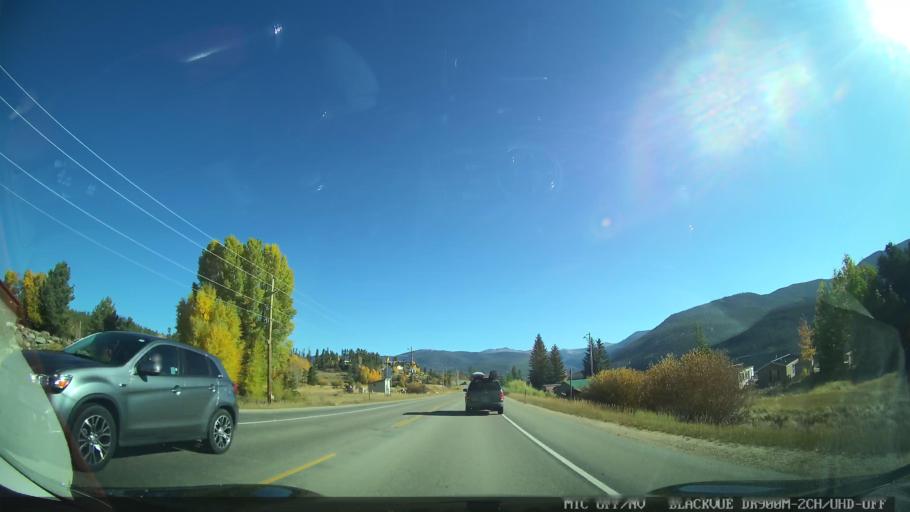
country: US
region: Colorado
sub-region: Grand County
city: Granby
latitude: 40.2238
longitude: -105.8545
